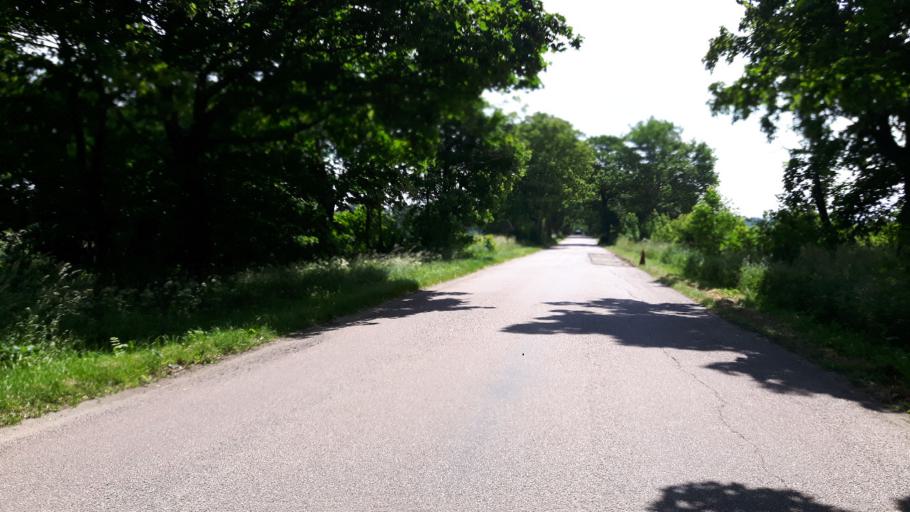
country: PL
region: Pomeranian Voivodeship
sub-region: Powiat wejherowski
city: Choczewo
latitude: 54.7442
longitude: 17.8099
